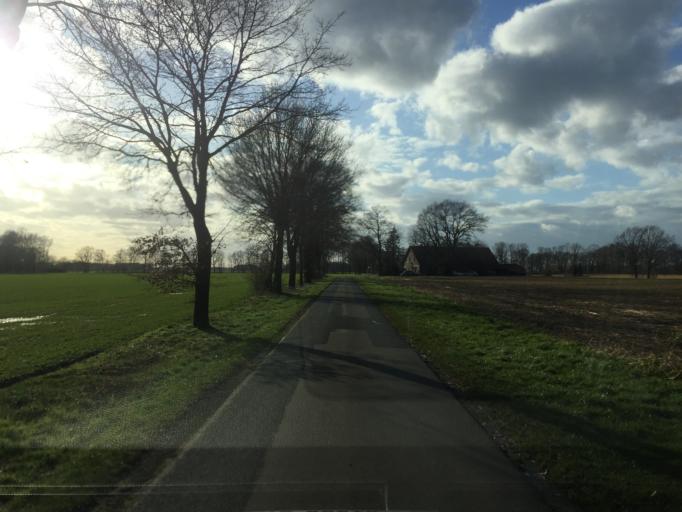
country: DE
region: Lower Saxony
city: Steyerberg
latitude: 52.5489
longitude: 9.0135
